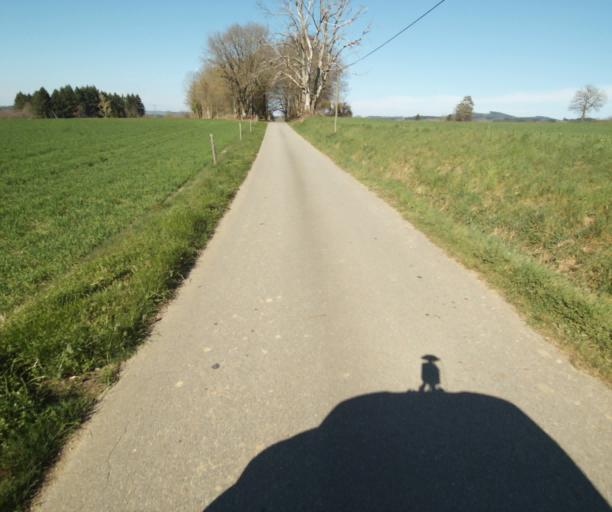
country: FR
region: Limousin
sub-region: Departement de la Correze
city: Chamboulive
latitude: 45.4789
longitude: 1.7390
